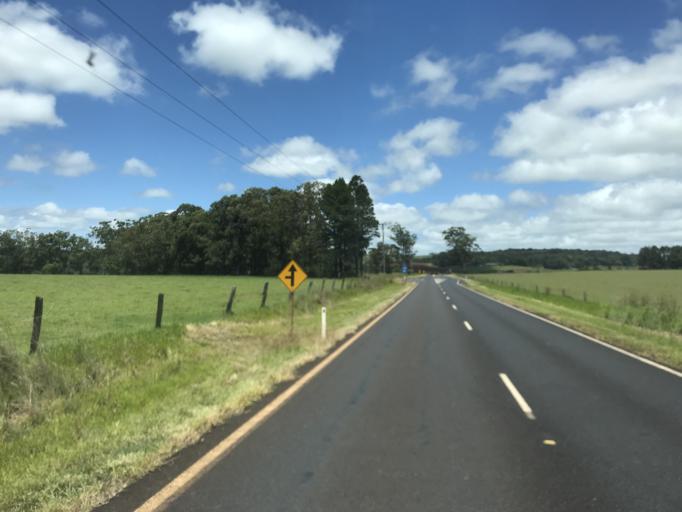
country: AU
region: Queensland
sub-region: Tablelands
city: Ravenshoe
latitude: -17.5104
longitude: 145.4540
